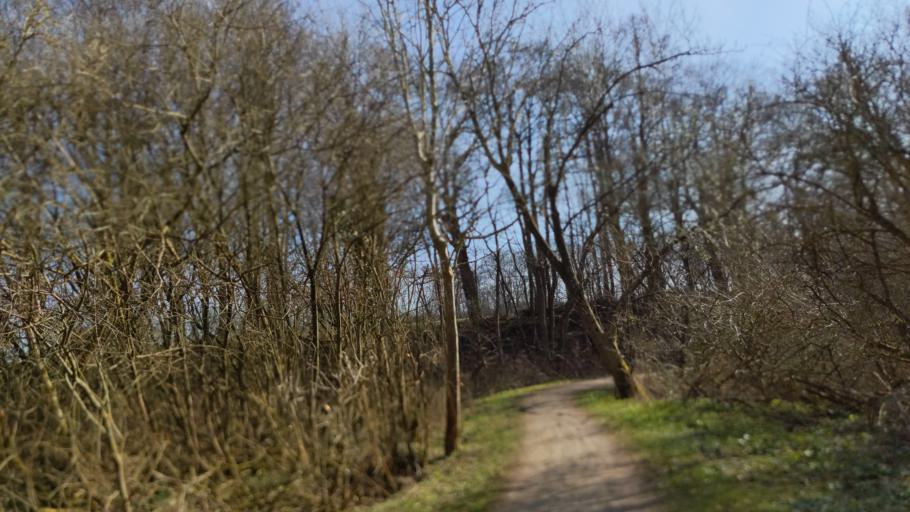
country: DE
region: Schleswig-Holstein
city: Timmendorfer Strand
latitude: 53.9871
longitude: 10.8208
